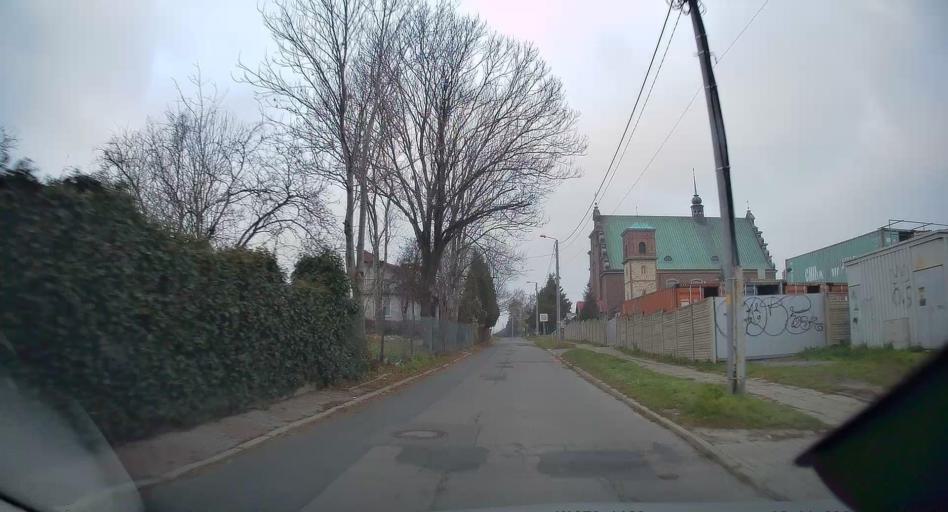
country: PL
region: Silesian Voivodeship
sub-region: Czestochowa
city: Czestochowa
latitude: 50.8171
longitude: 19.0941
